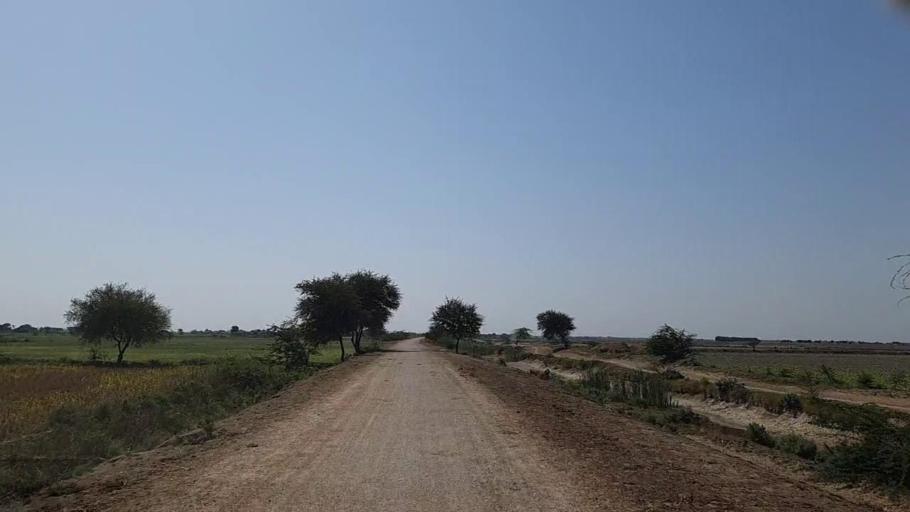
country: PK
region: Sindh
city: Mirpur Batoro
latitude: 24.6778
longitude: 68.3047
